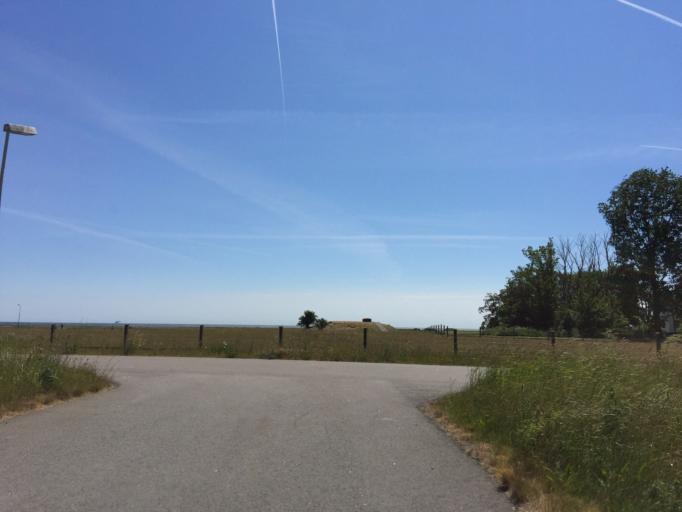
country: SE
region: Skane
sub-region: Trelleborgs Kommun
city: Skare
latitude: 55.3767
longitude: 13.0876
